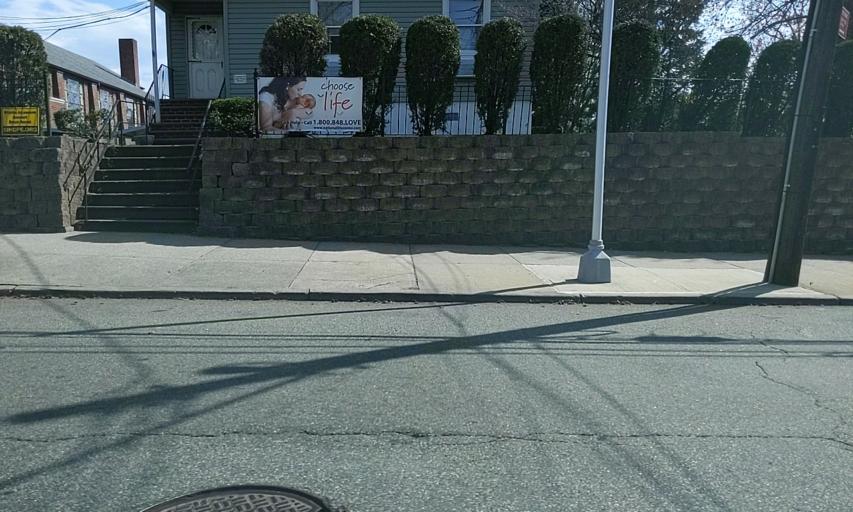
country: US
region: New York
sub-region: Richmond County
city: Staten Island
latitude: 40.6134
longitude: -74.1183
